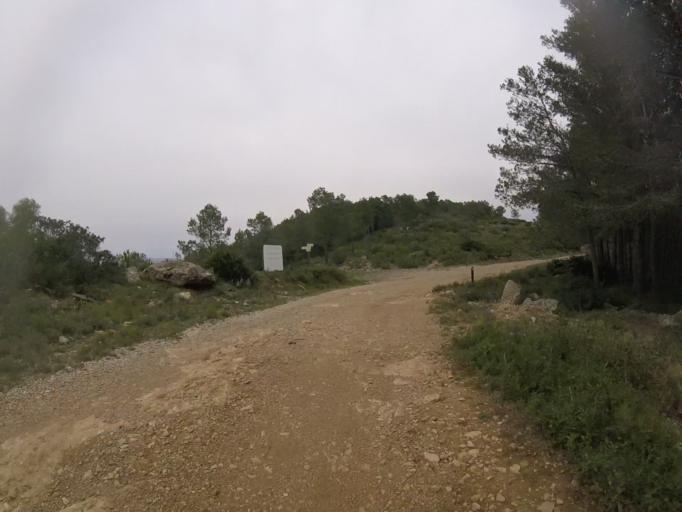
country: ES
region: Valencia
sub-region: Provincia de Castello
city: Alcala de Xivert
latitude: 40.3135
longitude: 0.2664
